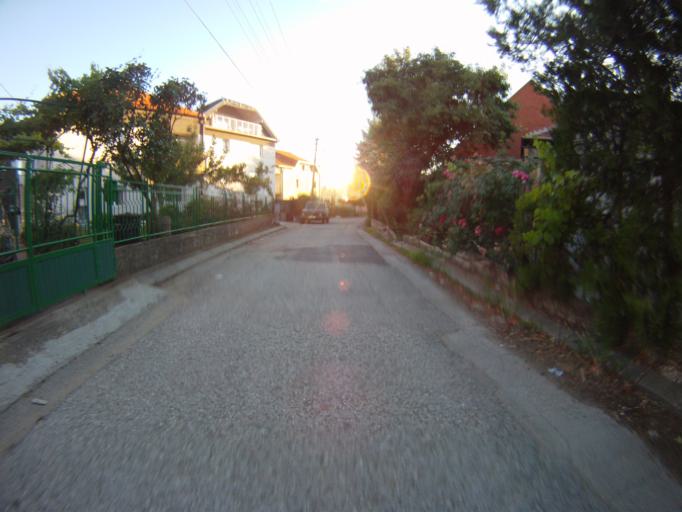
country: RS
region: Central Serbia
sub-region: Nisavski Okrug
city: Nis
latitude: 43.3103
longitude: 21.9159
